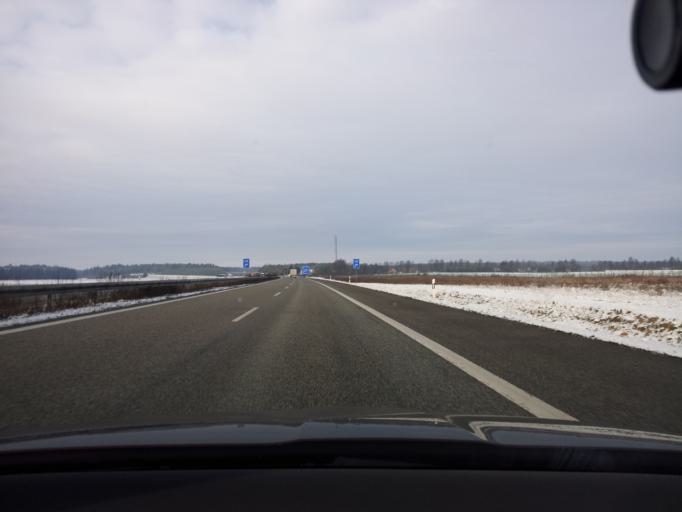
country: DE
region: Mecklenburg-Vorpommern
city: Sulstorf
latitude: 53.4823
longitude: 11.2854
